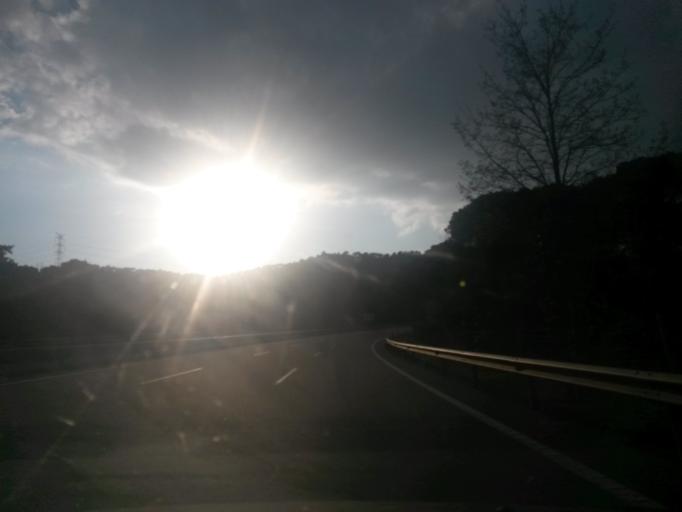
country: ES
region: Catalonia
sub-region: Provincia de Barcelona
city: Sant Julia de Vilatorta
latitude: 41.8941
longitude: 2.3493
